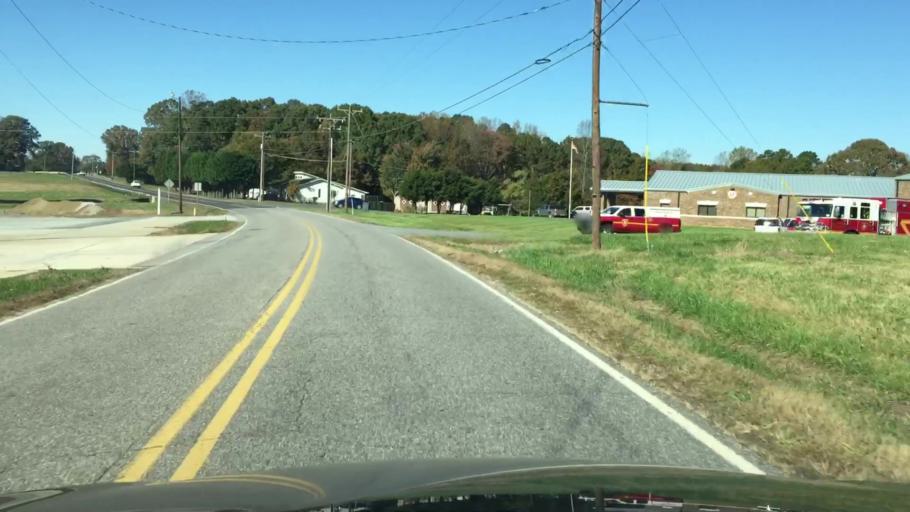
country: US
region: North Carolina
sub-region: Iredell County
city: Mooresville
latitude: 35.5671
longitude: -80.7751
